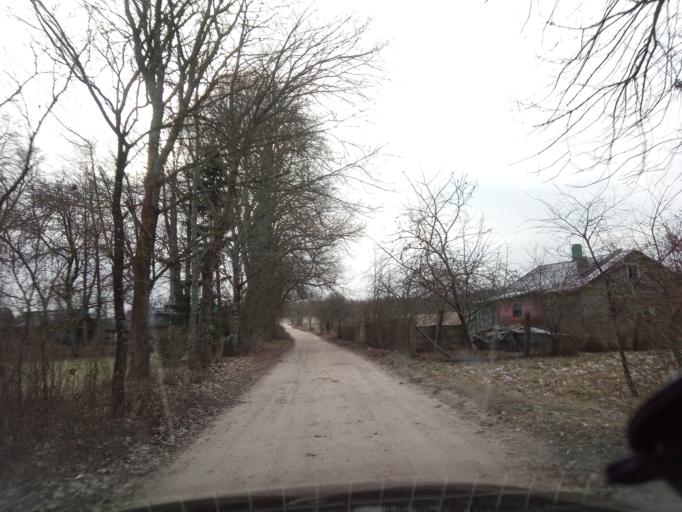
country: LT
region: Alytaus apskritis
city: Varena
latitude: 54.1249
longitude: 24.6467
